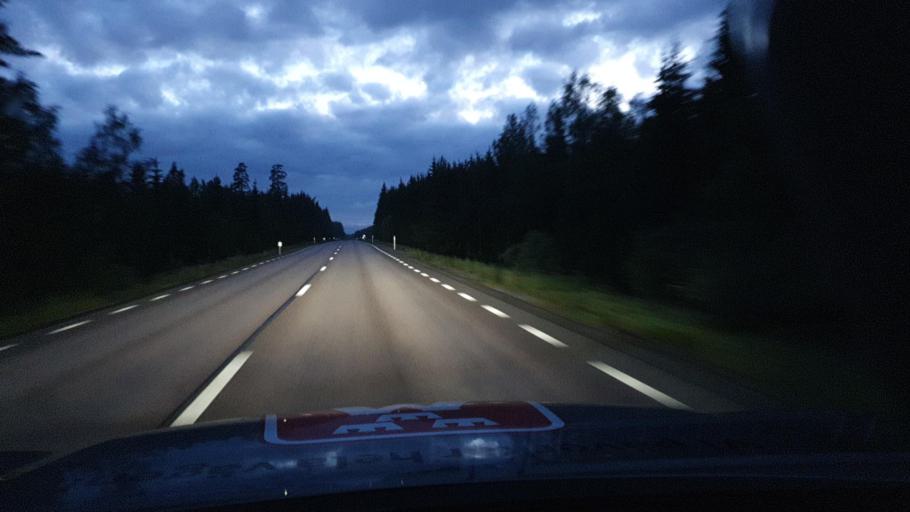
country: SE
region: Vaermland
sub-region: Storfors Kommun
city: Storfors
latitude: 59.4592
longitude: 14.3594
